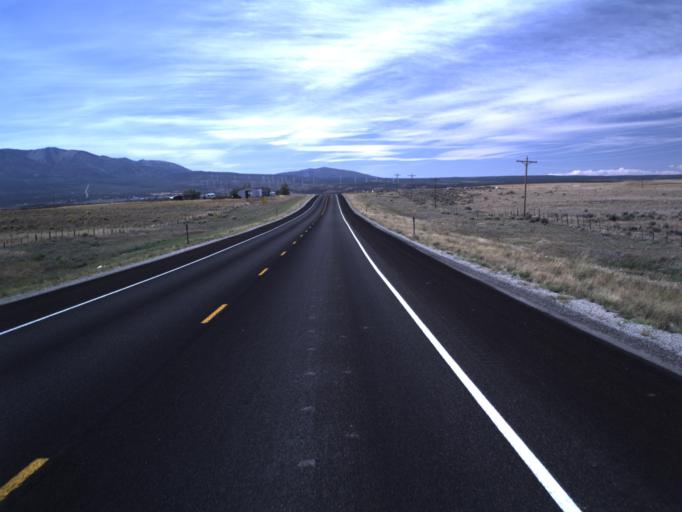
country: US
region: Utah
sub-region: San Juan County
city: Monticello
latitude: 37.8671
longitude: -109.2384
